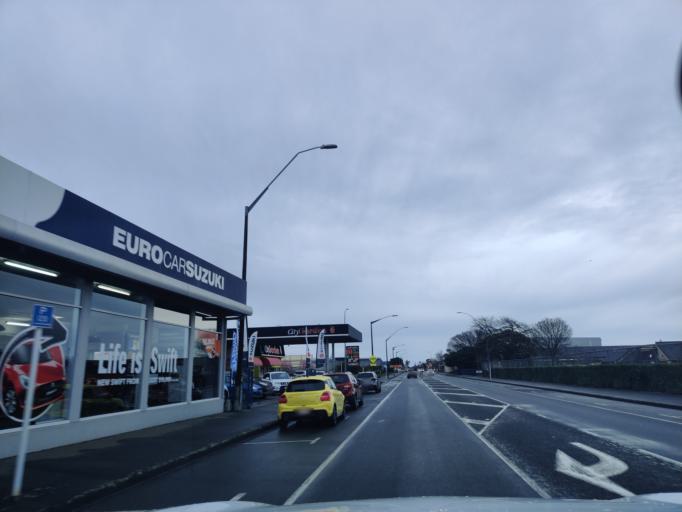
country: NZ
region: Manawatu-Wanganui
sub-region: Palmerston North City
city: Palmerston North
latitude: -40.3483
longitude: 175.6099
